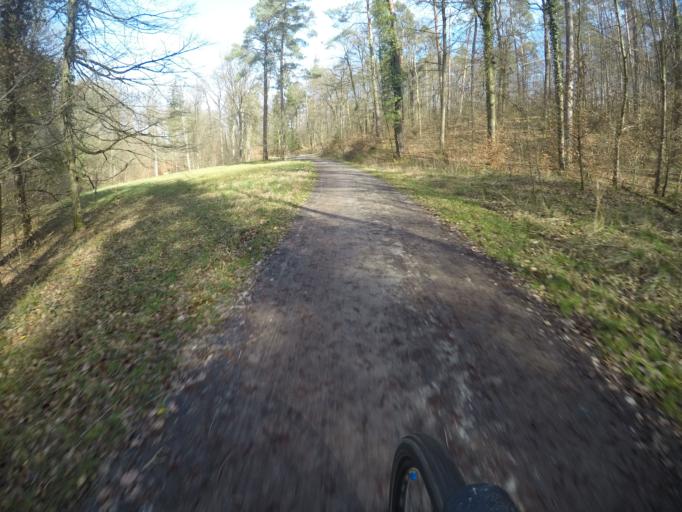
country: DE
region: Baden-Wuerttemberg
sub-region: Regierungsbezirk Stuttgart
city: Gerlingen
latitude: 48.7876
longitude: 9.1047
